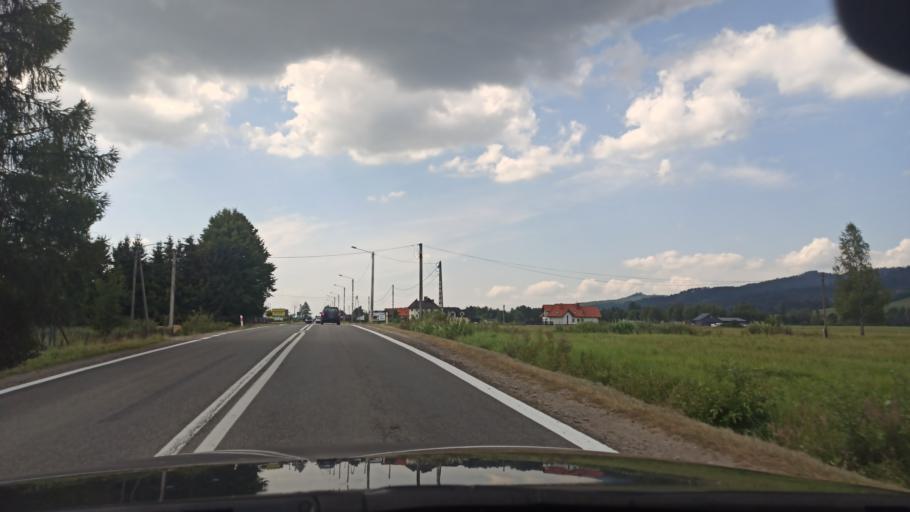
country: PL
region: Lesser Poland Voivodeship
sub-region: Powiat nowotarski
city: Lopuszna
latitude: 49.4718
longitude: 20.1227
